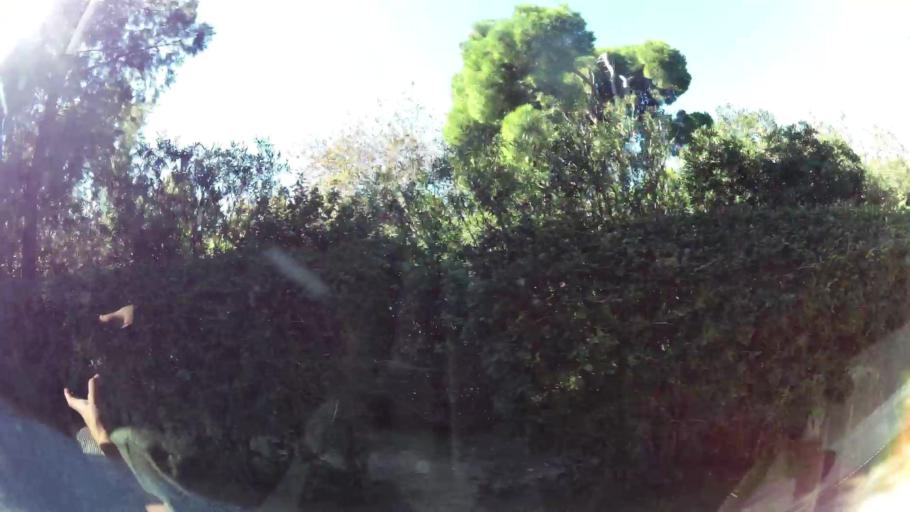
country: GR
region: Attica
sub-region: Nomarchia Athinas
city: Khalandrion
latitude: 38.0307
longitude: 23.8141
